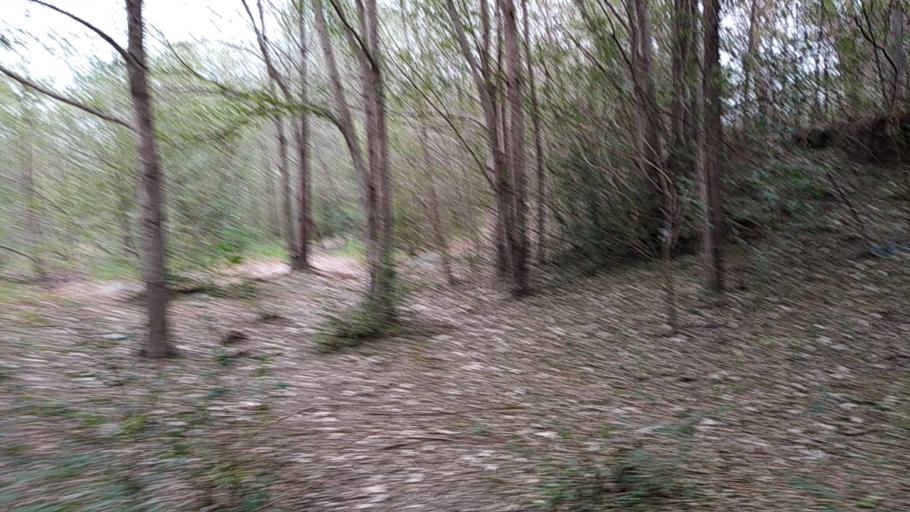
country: AR
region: Cordoba
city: Alta Gracia
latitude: -31.7221
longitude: -64.4117
